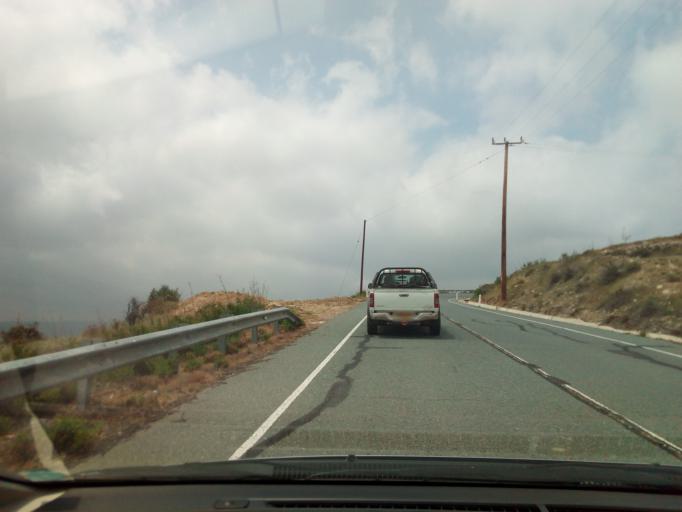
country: CY
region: Limassol
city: Pissouri
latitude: 34.7964
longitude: 32.6471
